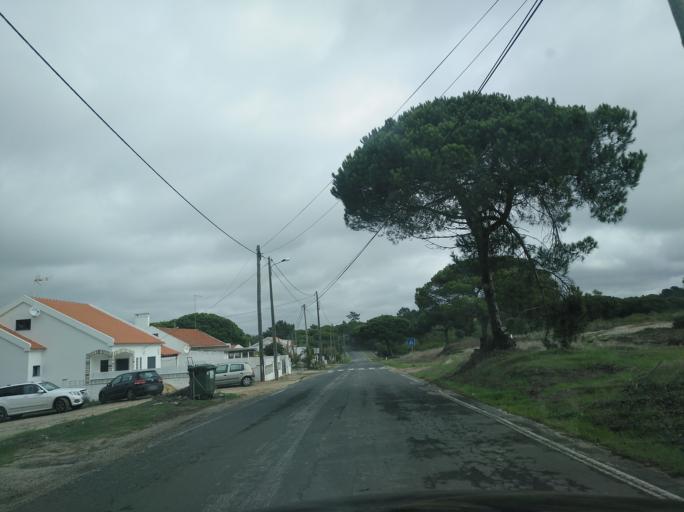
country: PT
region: Setubal
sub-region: Santiago do Cacem
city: Santo Andre
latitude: 38.1314
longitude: -8.7783
